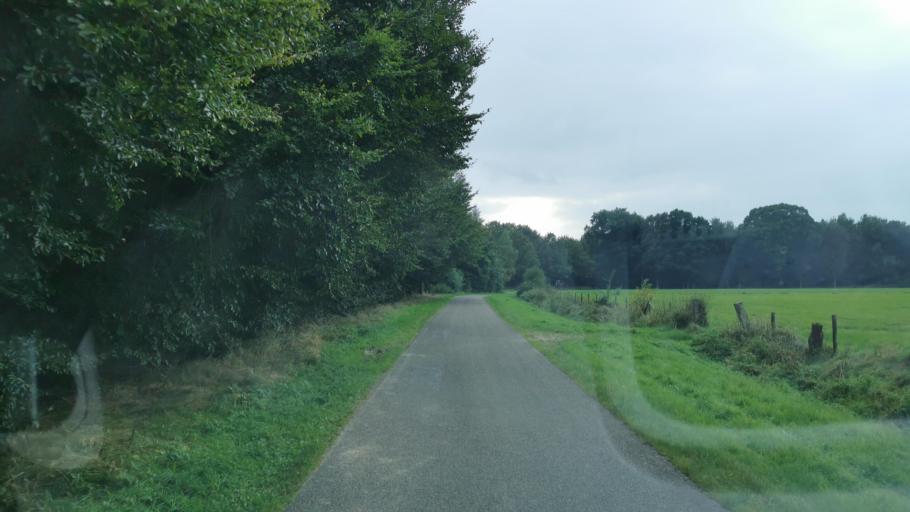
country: NL
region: Overijssel
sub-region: Gemeente Oldenzaal
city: Oldenzaal
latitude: 52.2998
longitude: 6.9677
